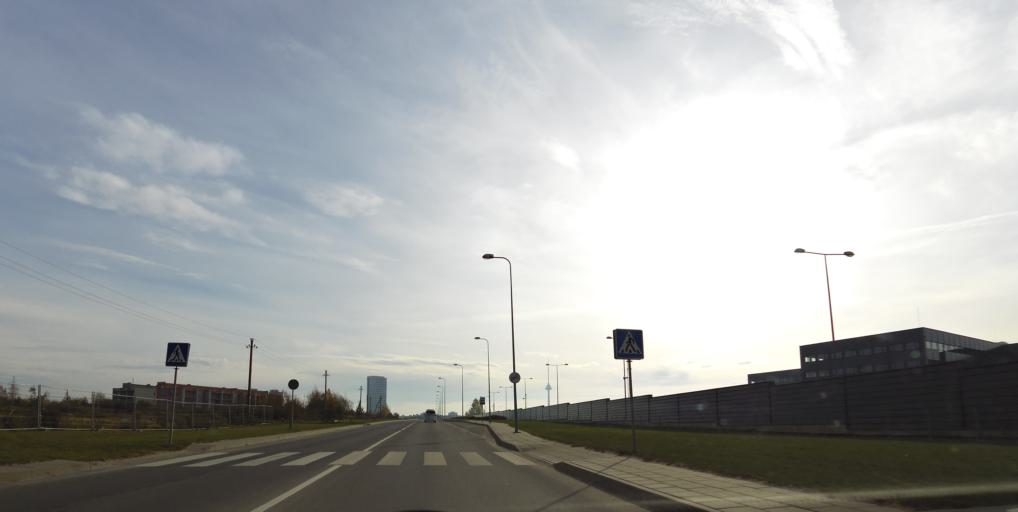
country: LT
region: Vilnius County
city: Justiniskes
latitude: 54.7085
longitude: 25.2030
